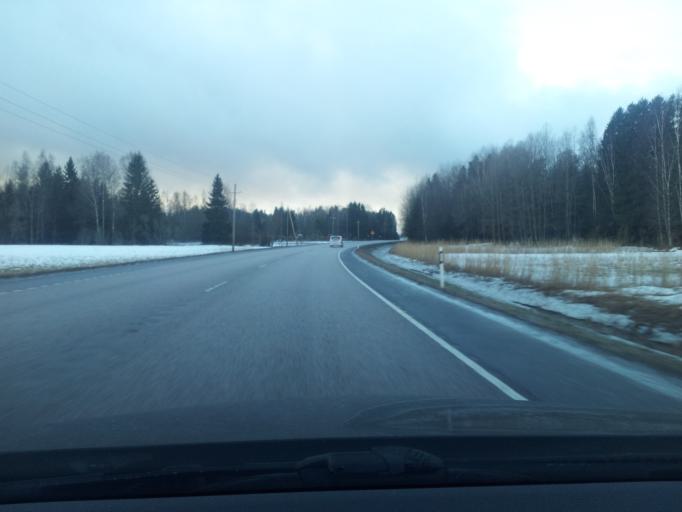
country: FI
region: Uusimaa
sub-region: Helsinki
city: Espoo
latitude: 60.1734
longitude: 24.5573
